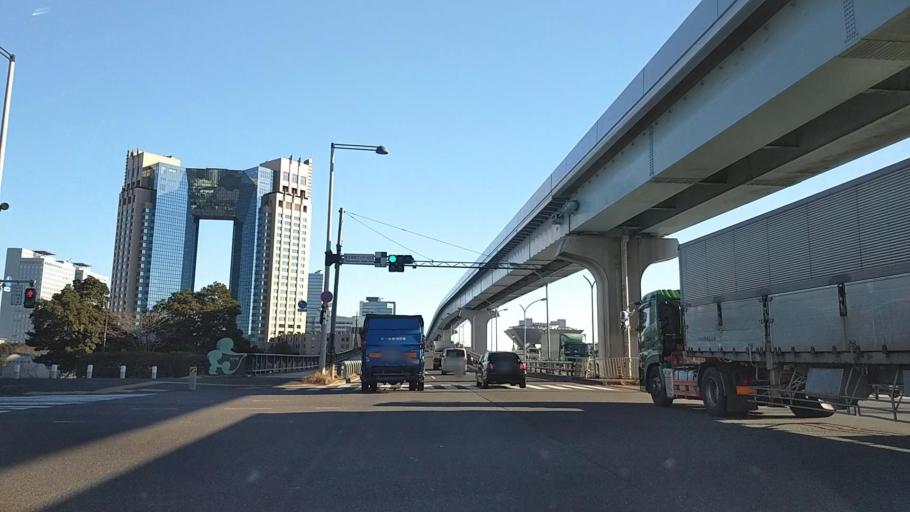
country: JP
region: Tokyo
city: Tokyo
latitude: 35.6265
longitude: 139.7842
